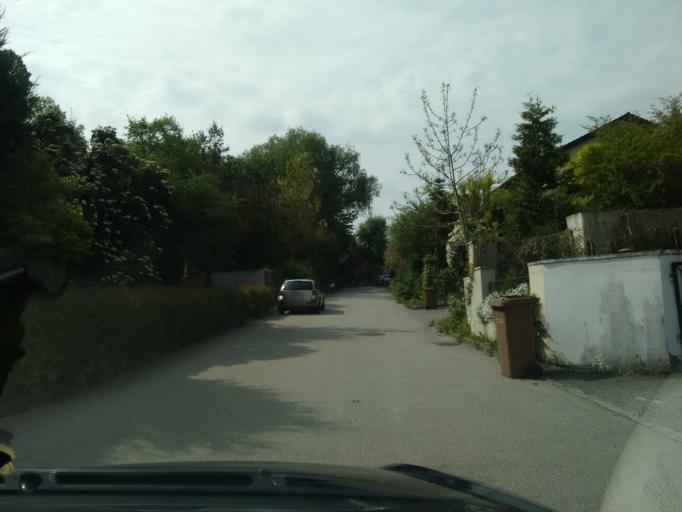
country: AT
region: Upper Austria
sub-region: Wels-Land
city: Marchtrenk
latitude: 48.1611
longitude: 14.0915
